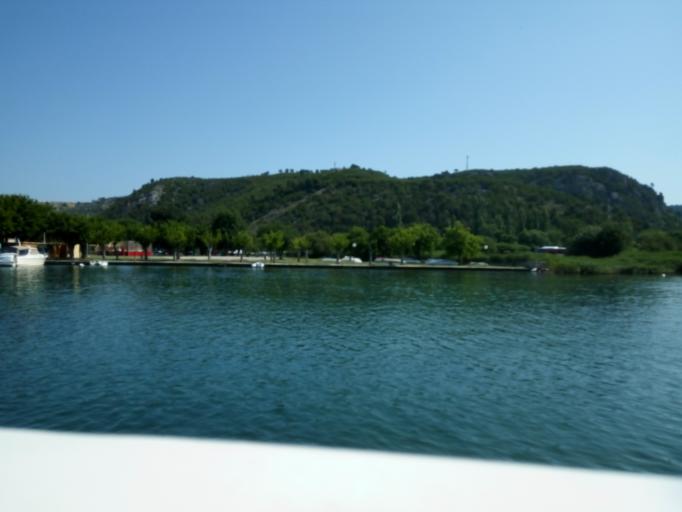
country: HR
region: Sibensko-Kniniska
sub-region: Grad Sibenik
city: Sibenik
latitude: 43.8157
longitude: 15.9235
